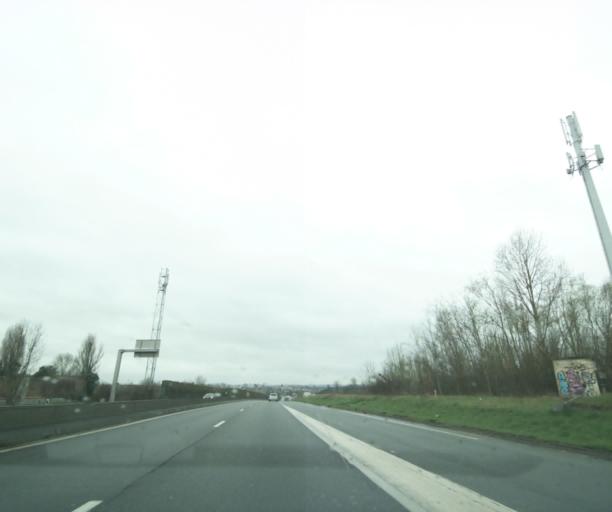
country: FR
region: Ile-de-France
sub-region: Departement de l'Essonne
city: Arpajon
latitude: 48.5965
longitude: 2.2439
